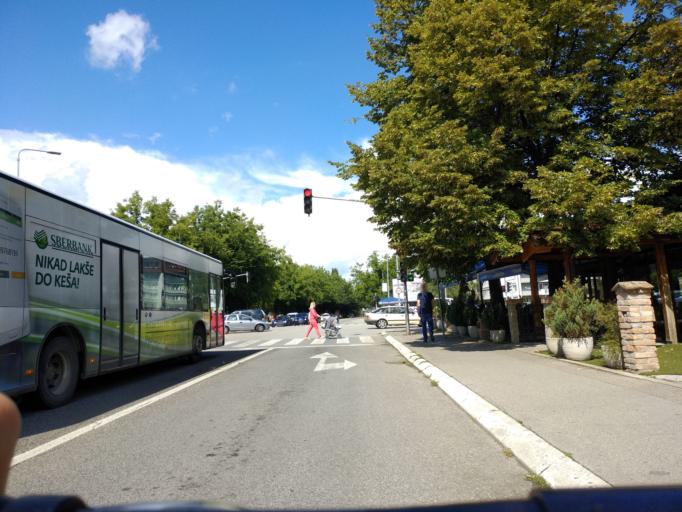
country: BA
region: Republika Srpska
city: Mejdan - Obilicevo
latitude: 44.7642
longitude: 17.2004
